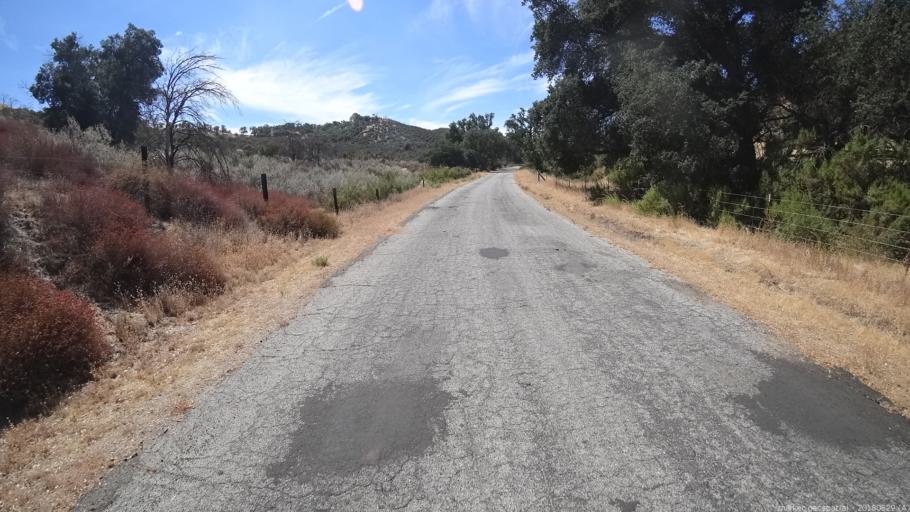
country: US
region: California
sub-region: San Luis Obispo County
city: Lake Nacimiento
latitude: 35.8488
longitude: -121.0357
